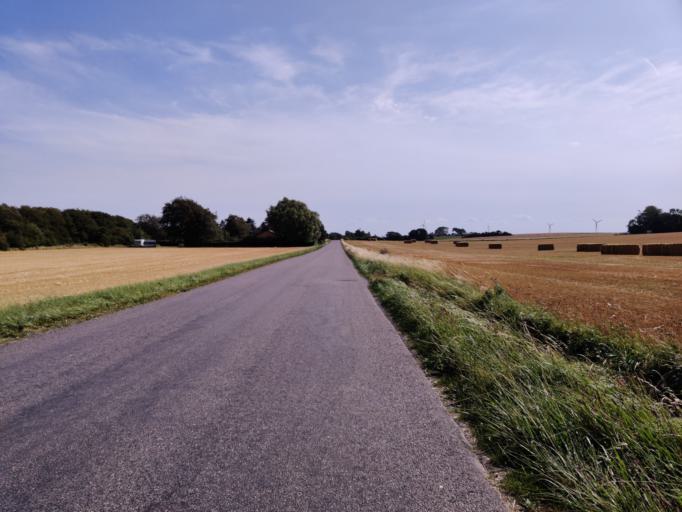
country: DK
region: Zealand
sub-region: Guldborgsund Kommune
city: Nykobing Falster
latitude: 54.6197
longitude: 11.9136
